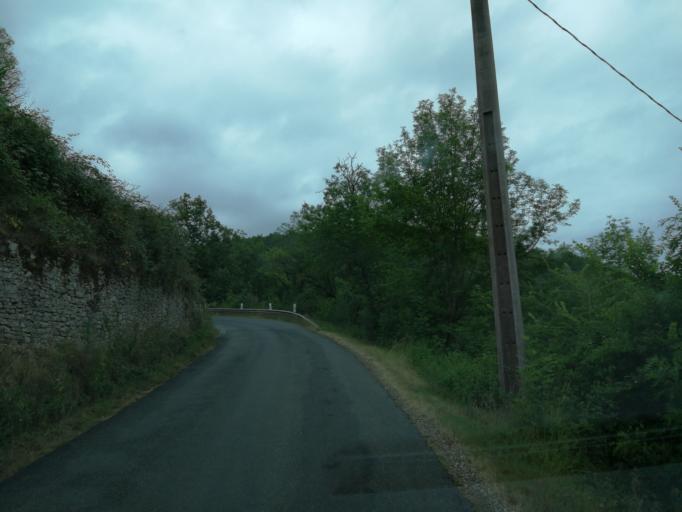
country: FR
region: Aquitaine
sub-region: Departement du Lot-et-Garonne
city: Montayral
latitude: 44.5416
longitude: 1.0708
